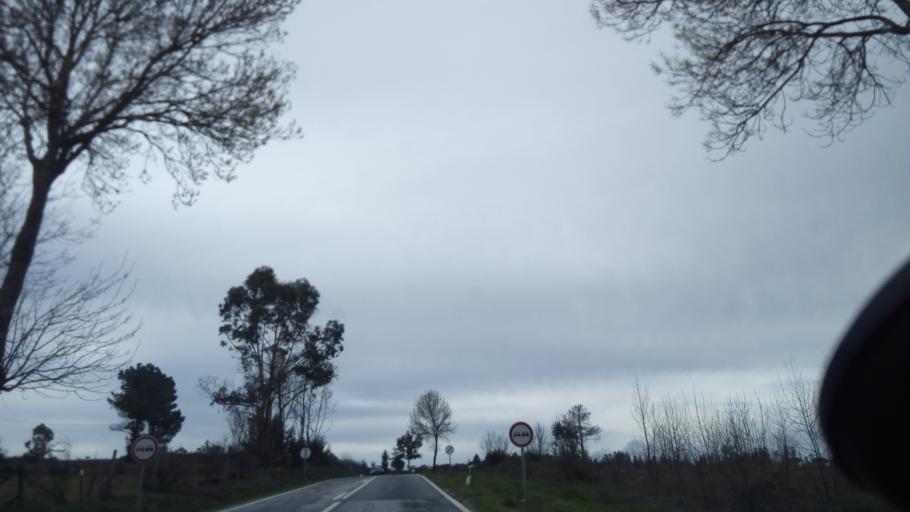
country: PT
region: Guarda
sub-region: Fornos de Algodres
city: Fornos de Algodres
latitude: 40.5270
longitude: -7.5899
